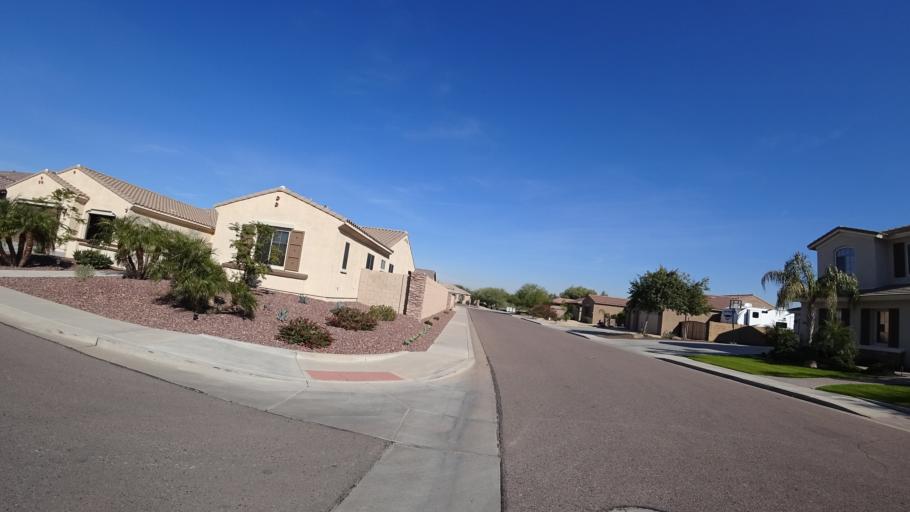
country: US
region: Arizona
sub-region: Maricopa County
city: Citrus Park
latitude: 33.5151
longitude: -112.4577
